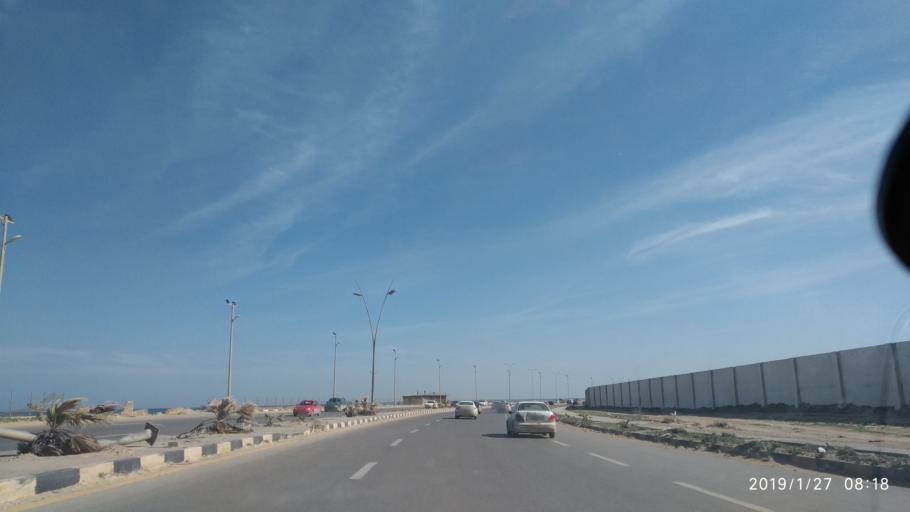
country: LY
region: Tripoli
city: Tagiura
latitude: 32.9087
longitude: 13.2867
